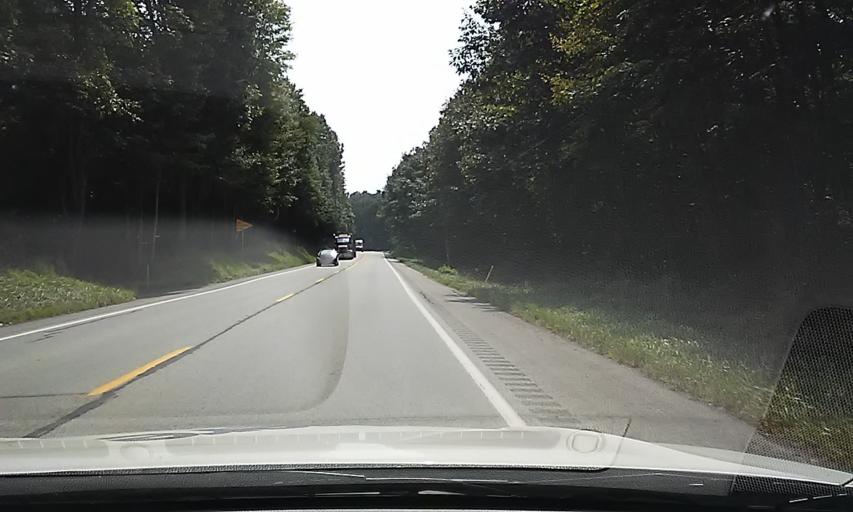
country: US
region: Pennsylvania
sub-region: Indiana County
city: Clymer
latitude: 40.7761
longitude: -79.0563
